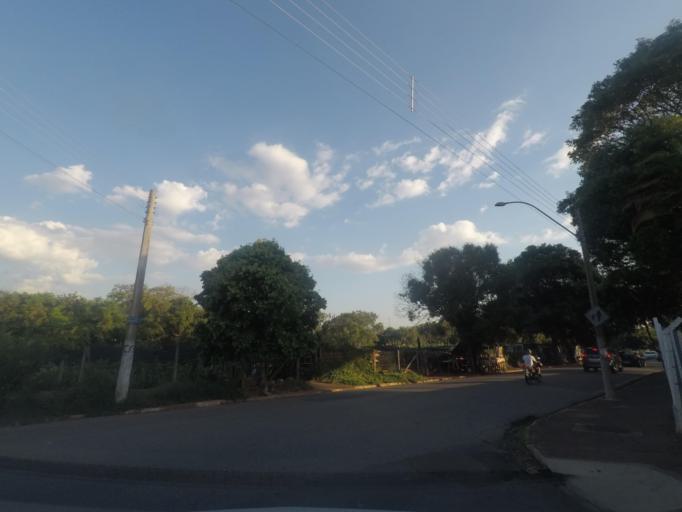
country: BR
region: Sao Paulo
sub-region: Sumare
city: Sumare
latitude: -22.8154
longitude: -47.2795
